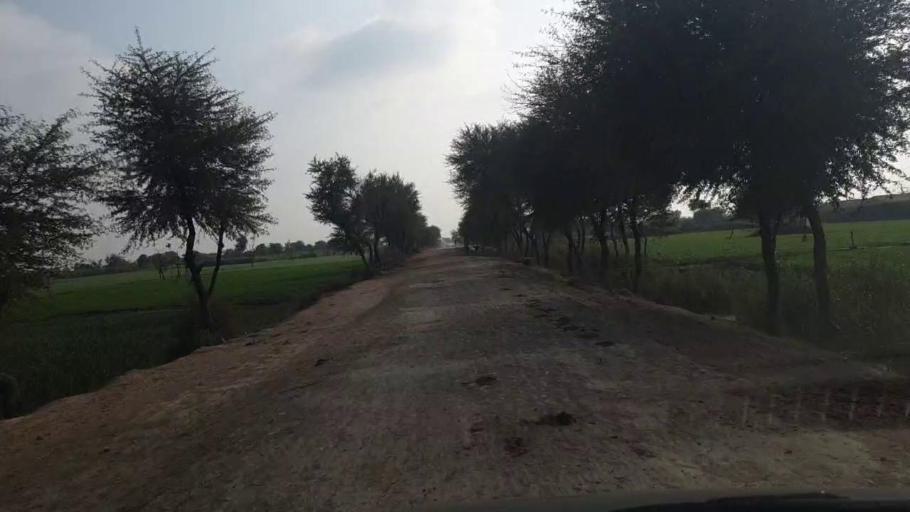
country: PK
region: Sindh
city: Shahdadpur
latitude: 25.8861
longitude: 68.6677
